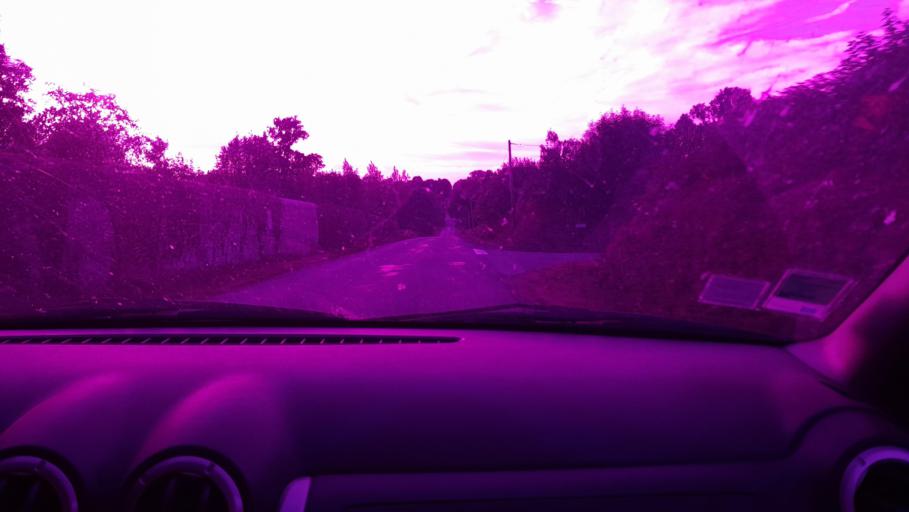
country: FR
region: Brittany
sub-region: Departement d'Ille-et-Vilaine
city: Le Pertre
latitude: 48.0405
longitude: -1.0436
